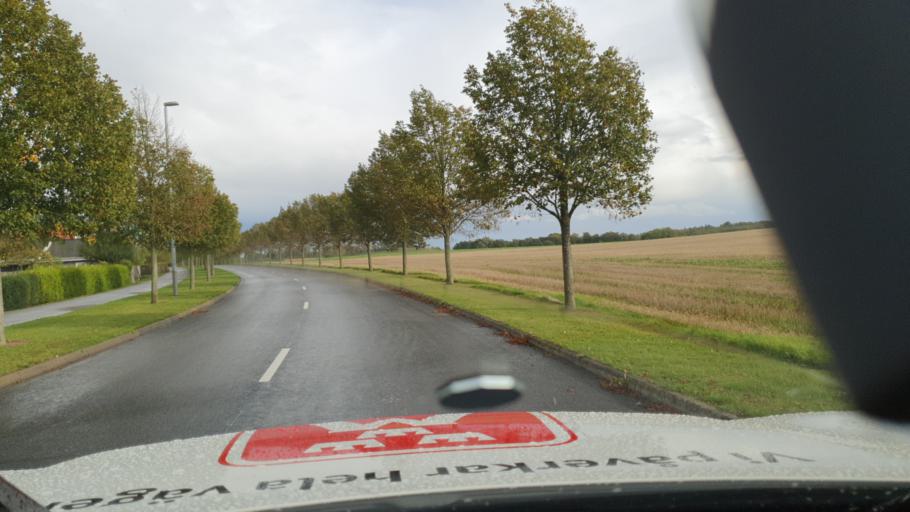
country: SE
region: Skane
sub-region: Malmo
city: Oxie
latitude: 55.5302
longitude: 13.0854
